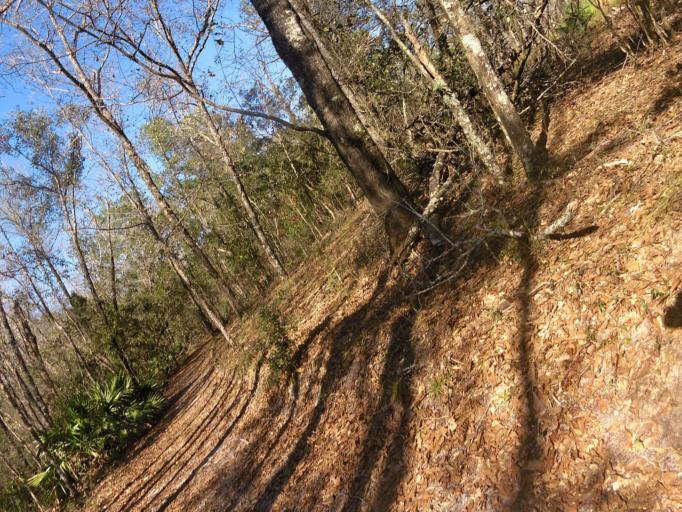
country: US
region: Florida
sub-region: Clay County
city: Middleburg
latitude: 30.1394
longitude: -81.8914
